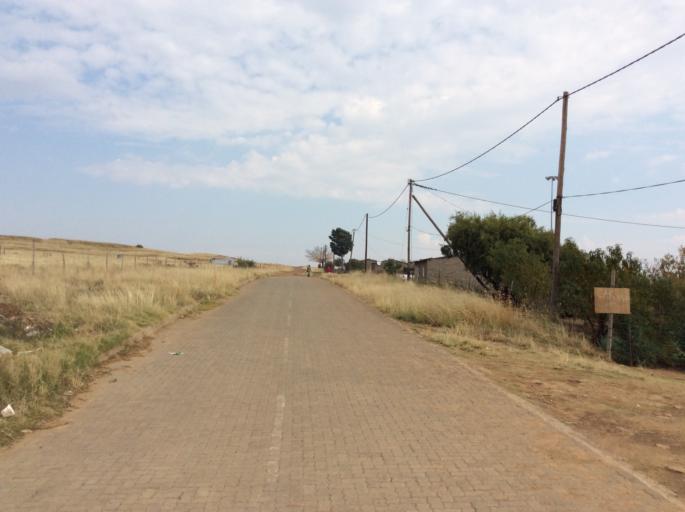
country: LS
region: Mafeteng
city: Mafeteng
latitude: -29.9856
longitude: 27.0062
